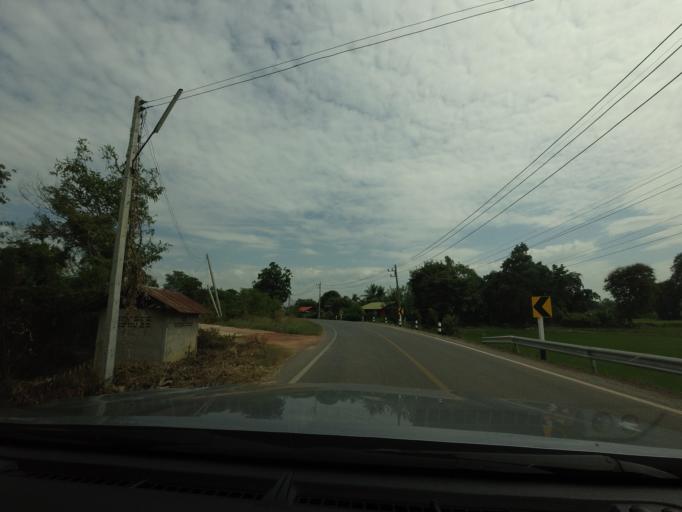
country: TH
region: Phitsanulok
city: Wang Thong
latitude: 16.7232
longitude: 100.3570
